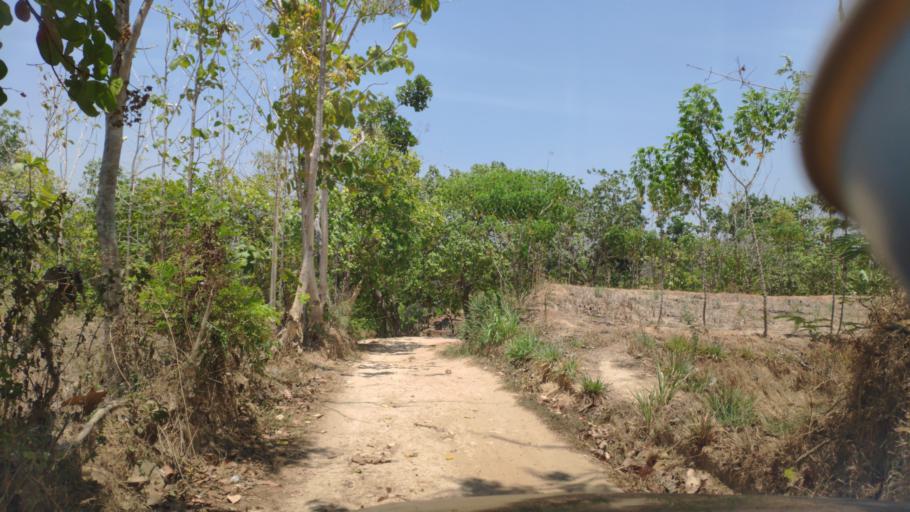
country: ID
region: Central Java
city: Ngapus
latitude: -6.9480
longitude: 111.1772
